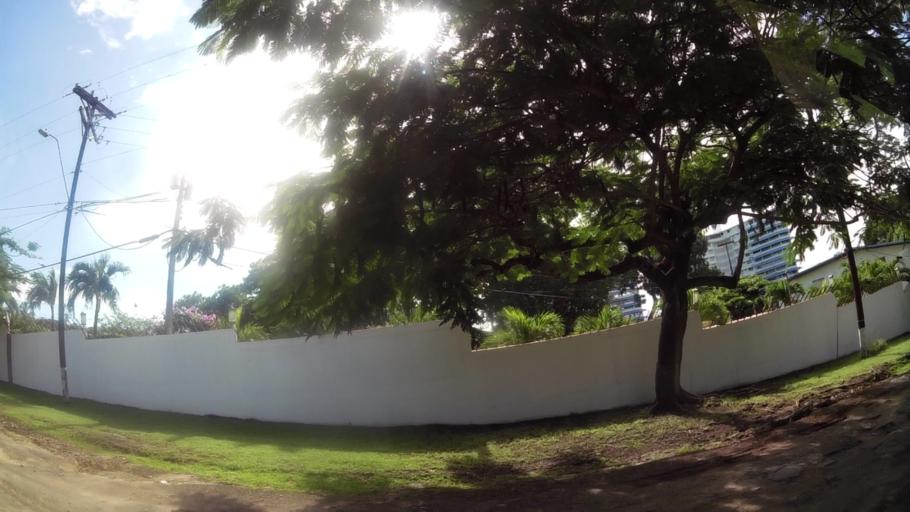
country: PA
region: Panama
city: Nueva Gorgona
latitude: 8.5263
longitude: -79.8934
